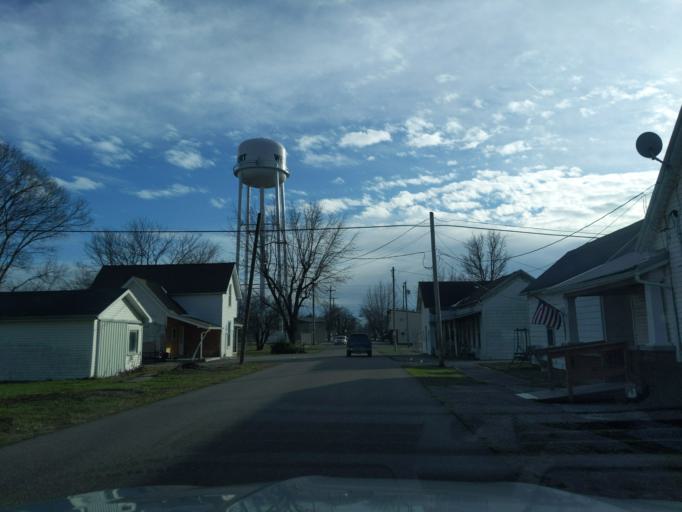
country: US
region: Indiana
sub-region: Decatur County
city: Westport
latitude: 39.1776
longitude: -85.5729
